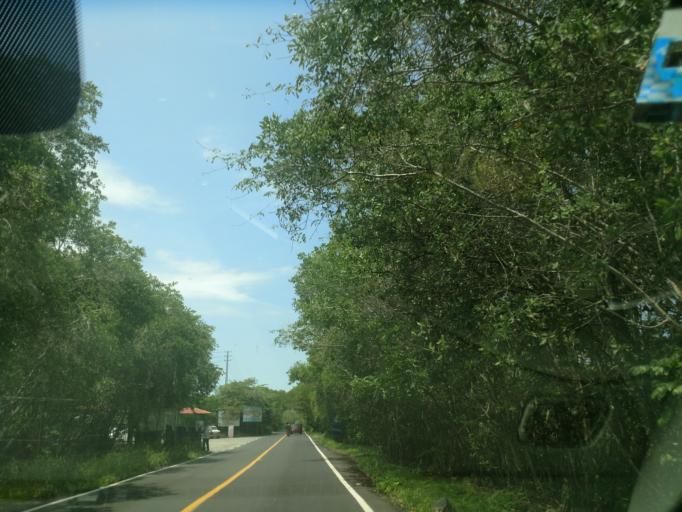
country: MX
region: Nayarit
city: San Blas
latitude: 21.5497
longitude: -105.2579
